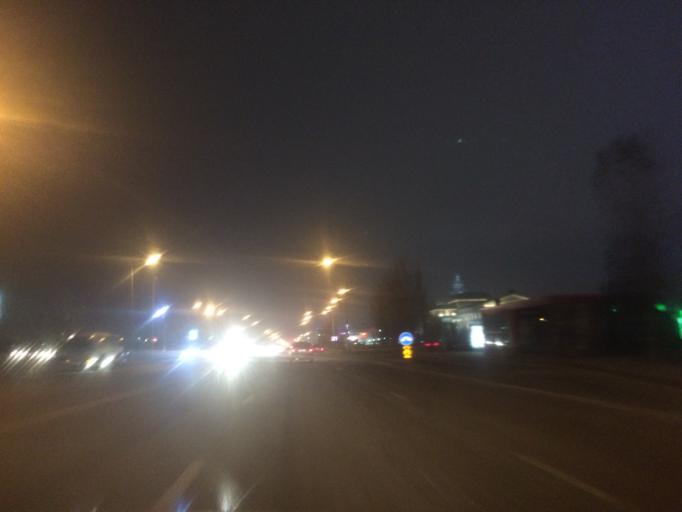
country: KZ
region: Astana Qalasy
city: Astana
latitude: 51.1307
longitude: 71.4062
